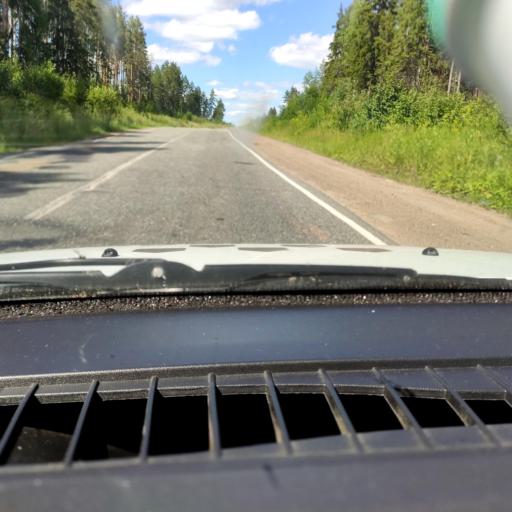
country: RU
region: Udmurtiya
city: Votkinsk
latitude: 57.0950
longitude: 54.0879
